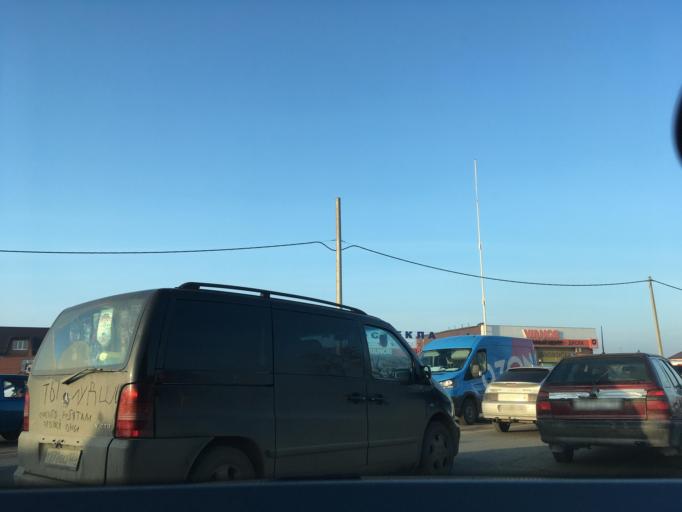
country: RU
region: Krasnodarskiy
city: Krasnodar
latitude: 45.1266
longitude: 39.0115
